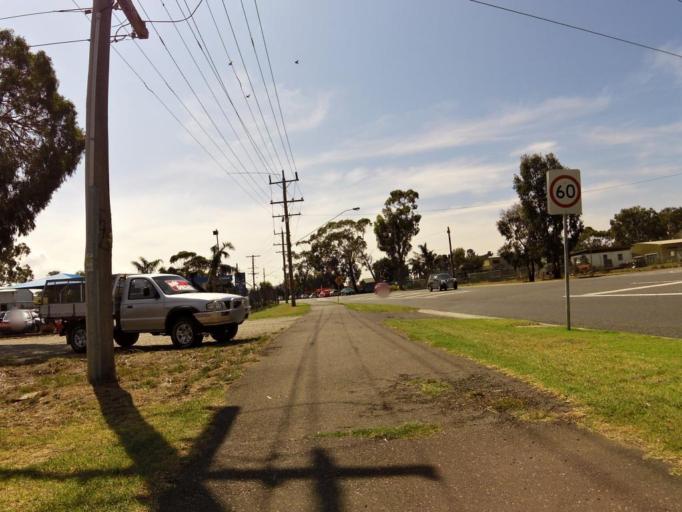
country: AU
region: Victoria
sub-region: Mornington Peninsula
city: Hastings
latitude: -38.2918
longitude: 145.1911
